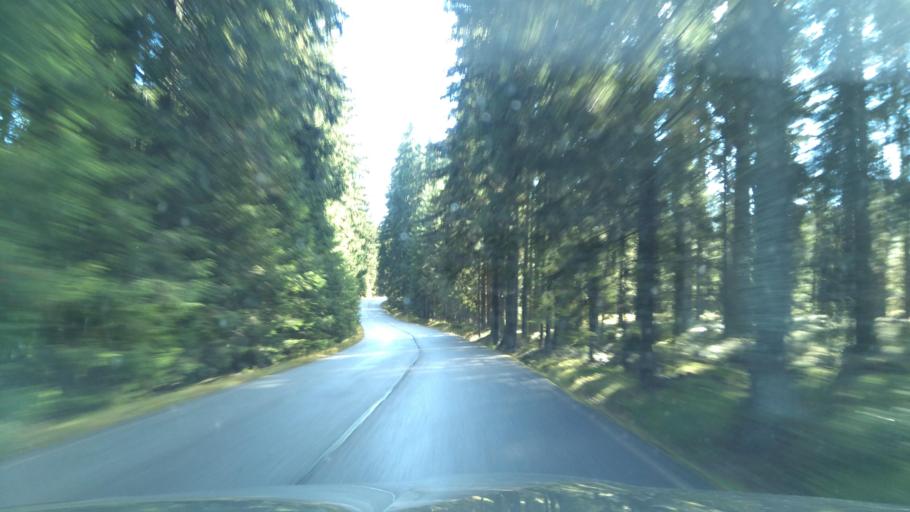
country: CZ
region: Jihocesky
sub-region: Okres Prachatice
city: Borova Lada
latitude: 49.0245
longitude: 13.5595
